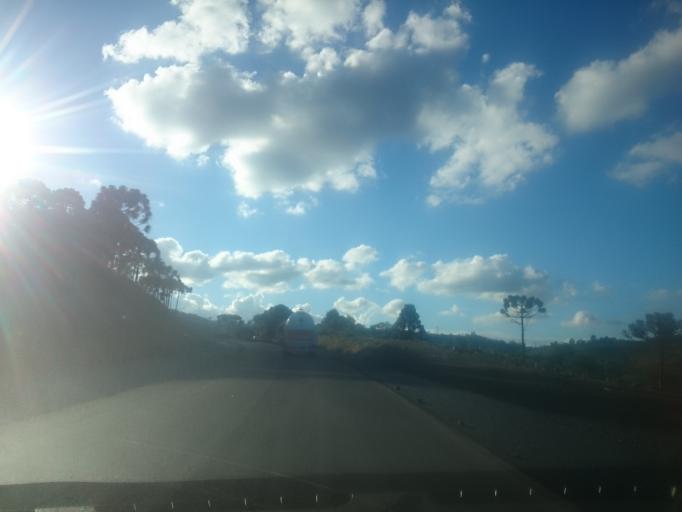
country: BR
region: Santa Catarina
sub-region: Sao Joaquim
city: Sao Joaquim
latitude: -28.0828
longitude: -50.0631
